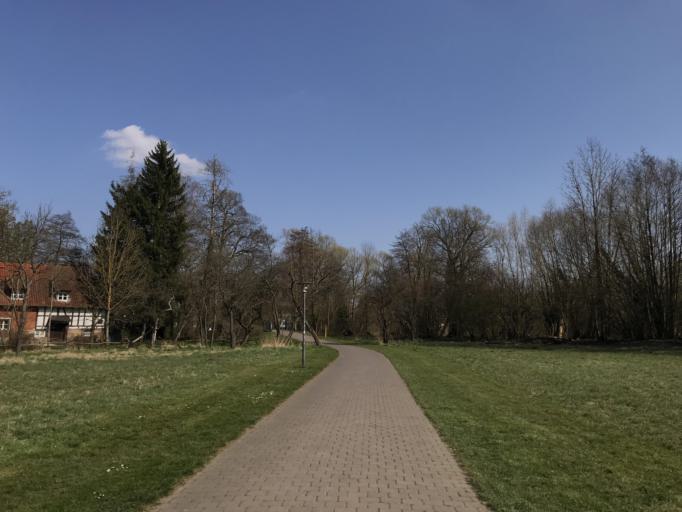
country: DE
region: Hesse
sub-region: Regierungsbezirk Kassel
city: Fulda
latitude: 50.5506
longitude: 9.6671
